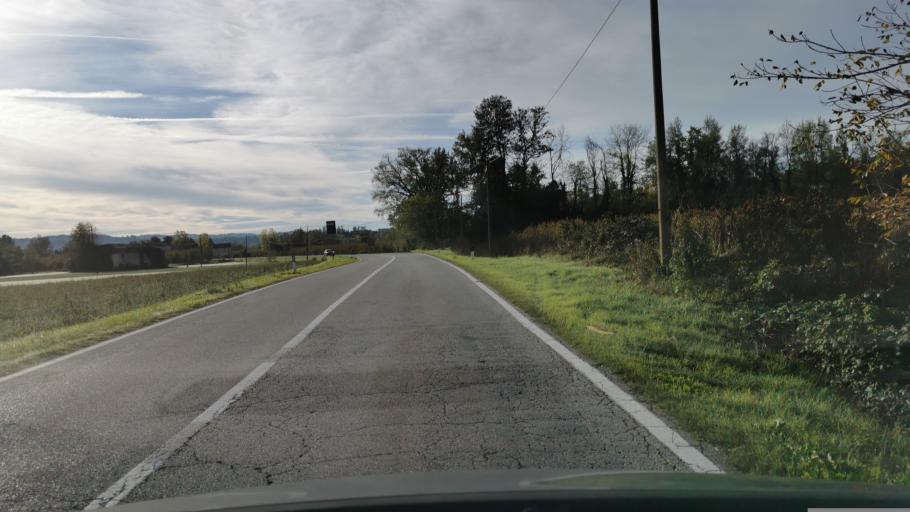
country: IT
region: Piedmont
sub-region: Provincia di Cuneo
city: Narzole
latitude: 44.5910
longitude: 7.8942
